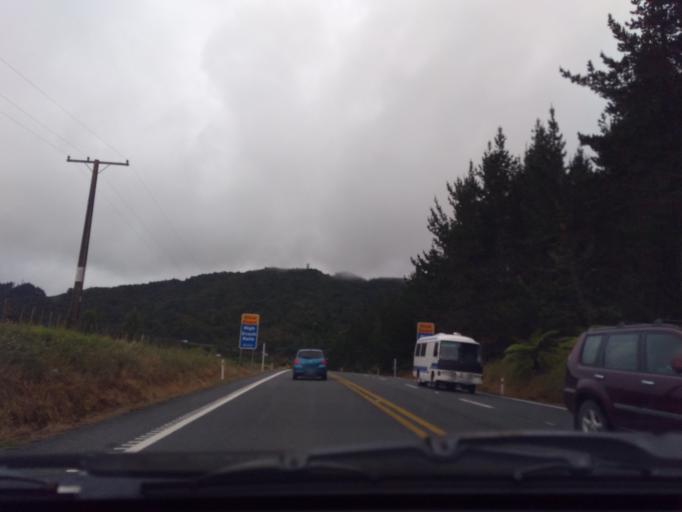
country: NZ
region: Northland
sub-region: Whangarei
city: Ruakaka
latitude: -36.0854
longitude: 174.4305
